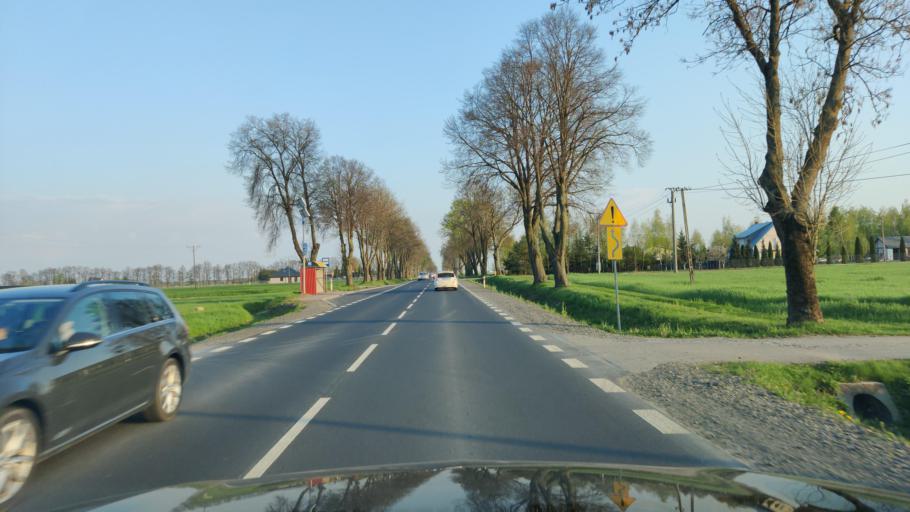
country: PL
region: Masovian Voivodeship
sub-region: Powiat pultuski
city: Pokrzywnica
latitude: 52.6228
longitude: 21.1007
